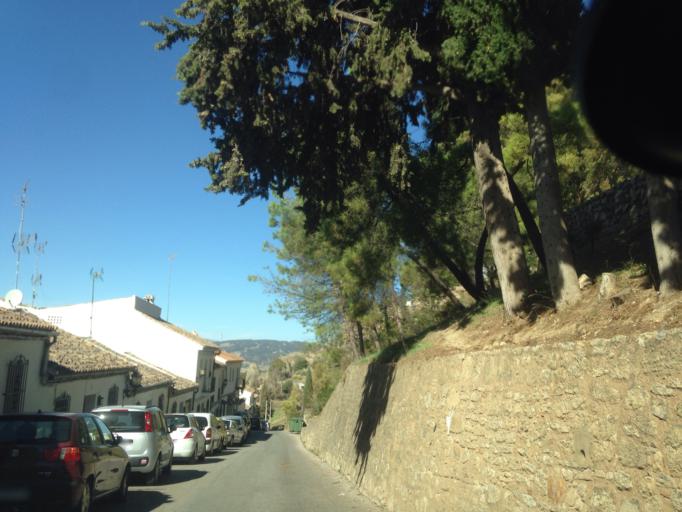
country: ES
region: Andalusia
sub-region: Provincia de Malaga
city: Ronda
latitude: 36.7345
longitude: -5.1651
